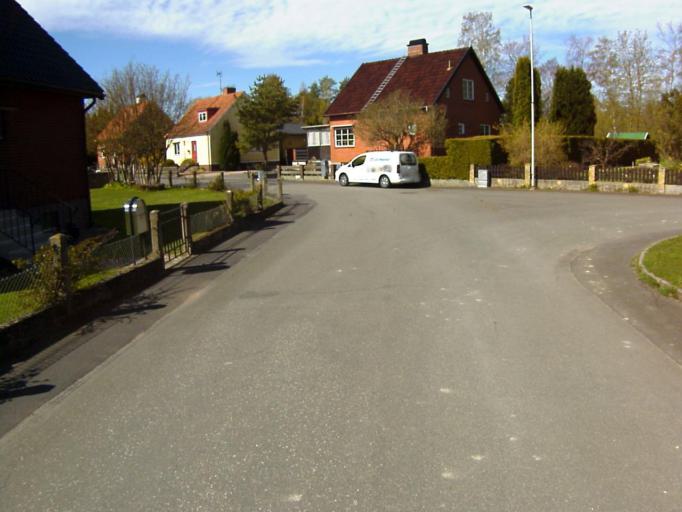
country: SE
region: Skane
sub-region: Kristianstads Kommun
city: Norra Asum
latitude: 55.9919
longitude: 14.1500
